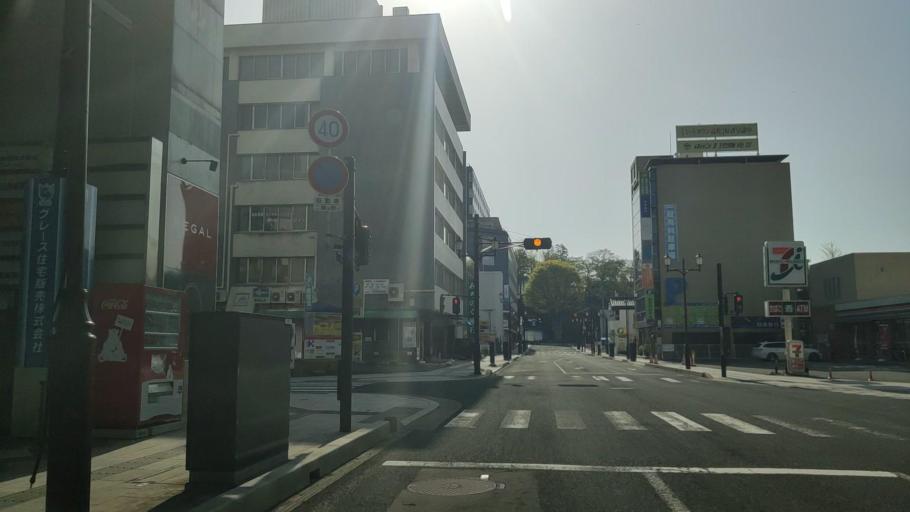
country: JP
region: Iwate
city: Morioka-shi
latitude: 39.7011
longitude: 141.1474
